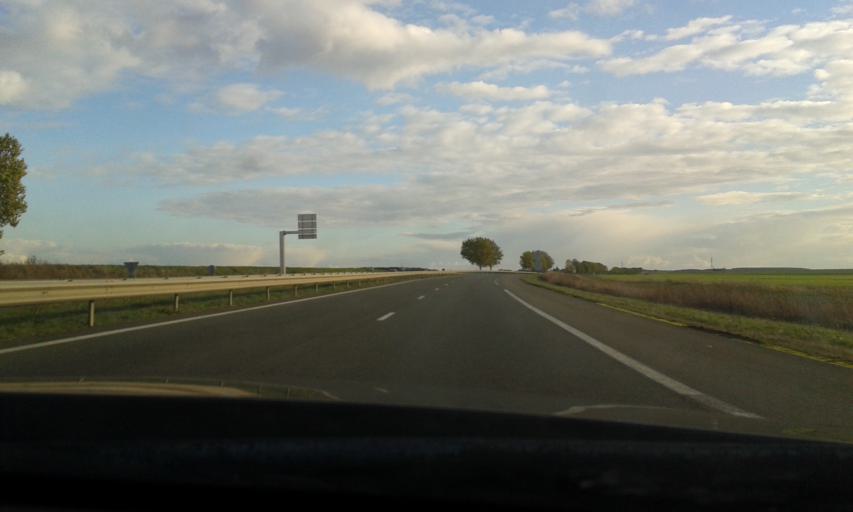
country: FR
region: Centre
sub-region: Departement d'Eure-et-Loir
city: Luray
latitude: 48.6706
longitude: 1.3875
